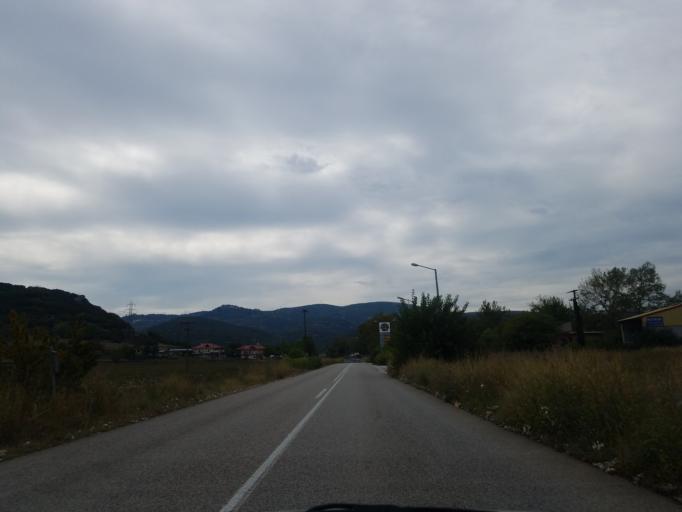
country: GR
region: Central Greece
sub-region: Nomos Fthiotidos
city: Domokos
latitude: 39.1595
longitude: 22.2934
